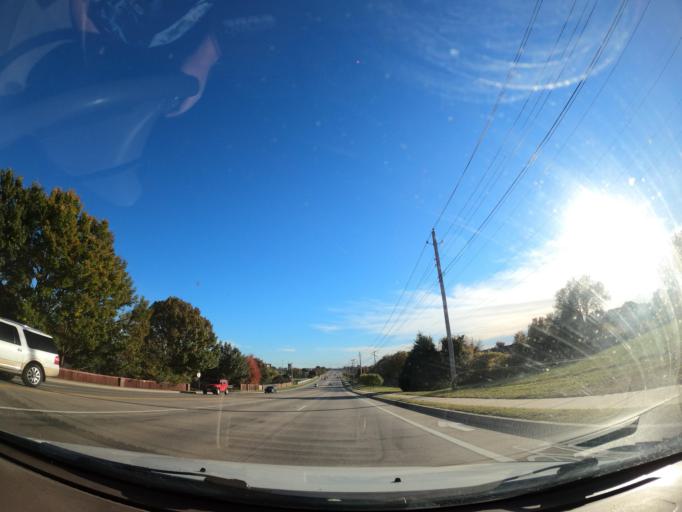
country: US
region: Oklahoma
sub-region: Tulsa County
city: Owasso
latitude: 36.2869
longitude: -95.8301
